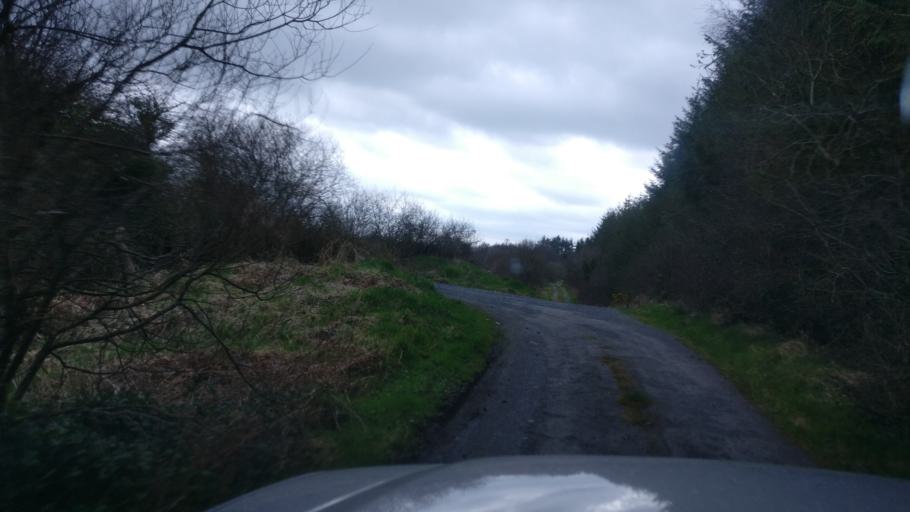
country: IE
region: Connaught
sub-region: County Galway
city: Loughrea
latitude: 53.2727
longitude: -8.4531
